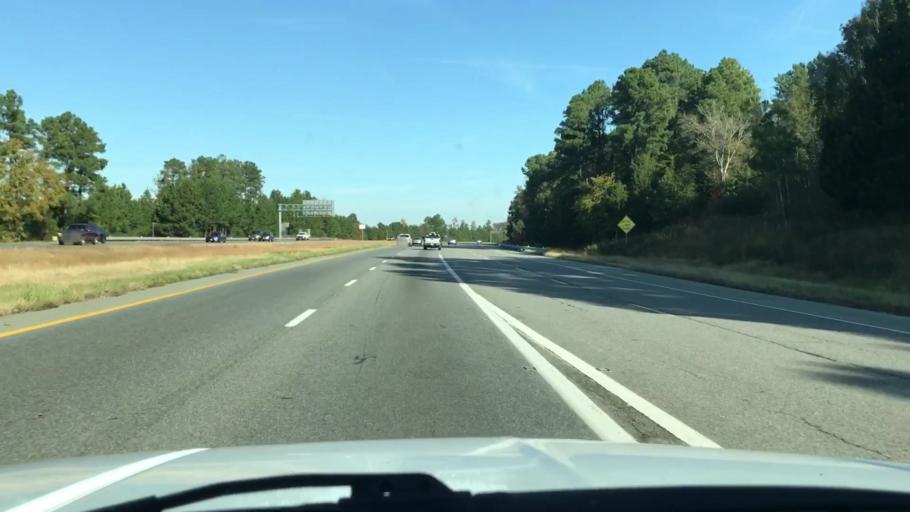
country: US
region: Virginia
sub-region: Henrico County
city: Short Pump
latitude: 37.6427
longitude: -77.6650
